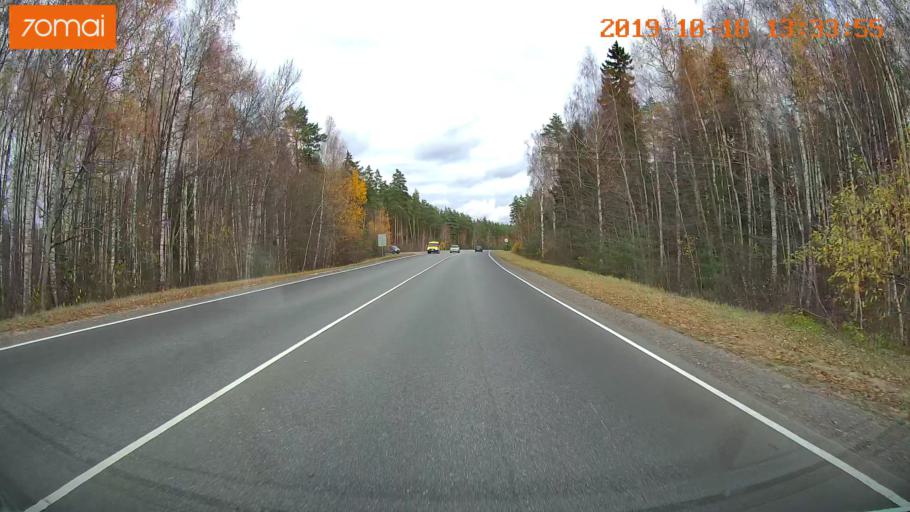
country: RU
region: Rjazan
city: Solotcha
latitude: 54.8492
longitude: 39.9440
